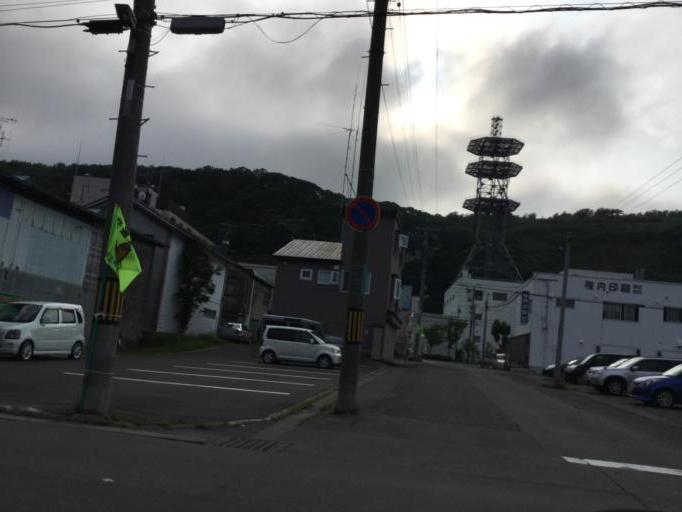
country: JP
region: Hokkaido
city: Wakkanai
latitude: 45.4139
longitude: 141.6753
